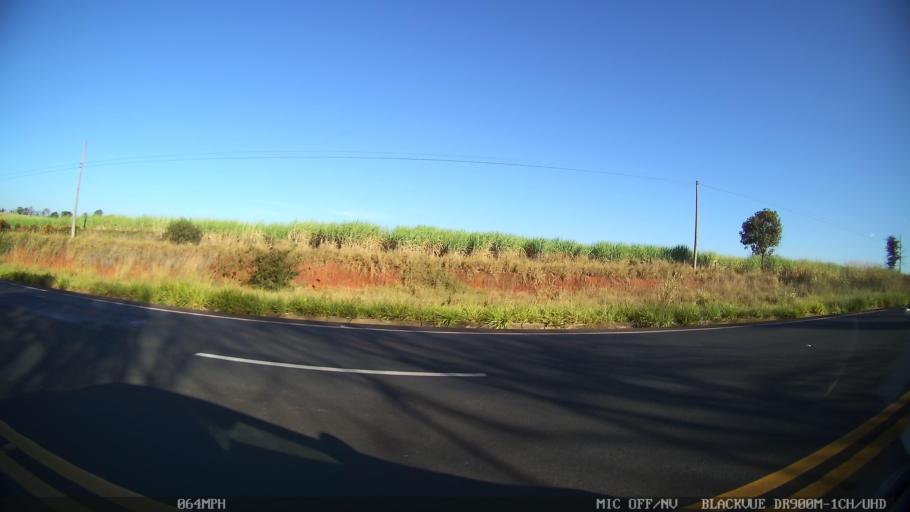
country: BR
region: Sao Paulo
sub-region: Olimpia
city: Olimpia
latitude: -20.7294
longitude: -49.0506
